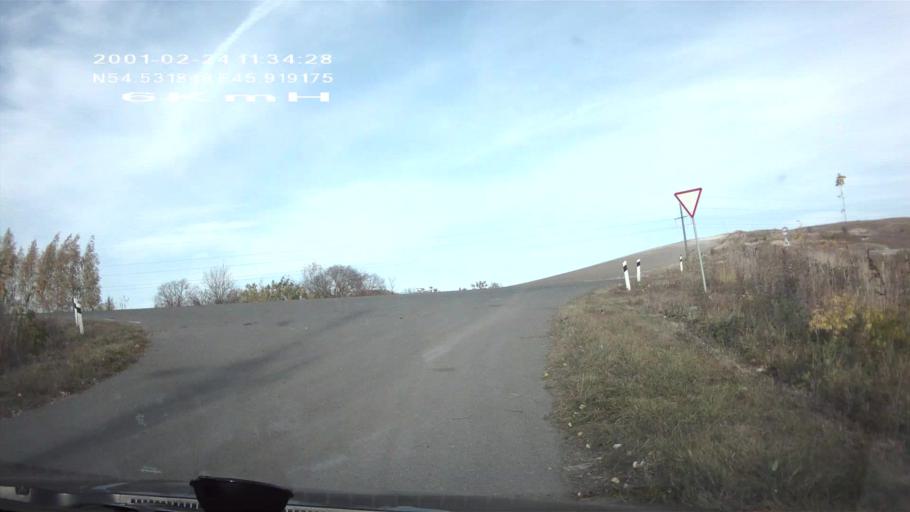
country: RU
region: Mordoviya
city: Atyashevo
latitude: 54.5323
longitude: 45.9185
